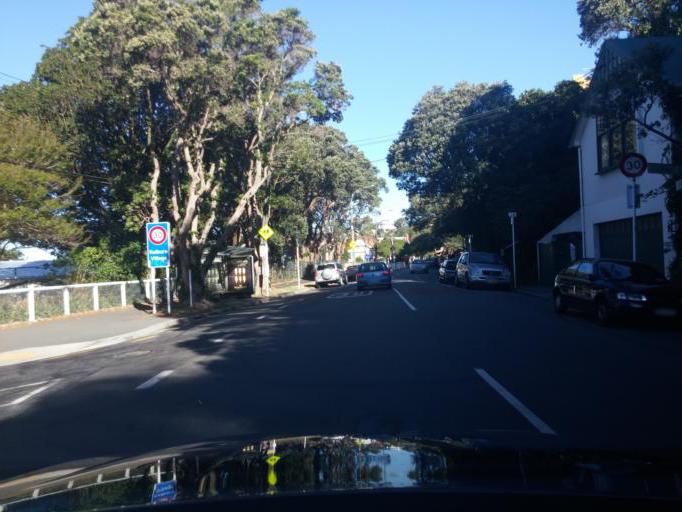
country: NZ
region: Wellington
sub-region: Wellington City
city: Kelburn
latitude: -41.2869
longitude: 174.7605
